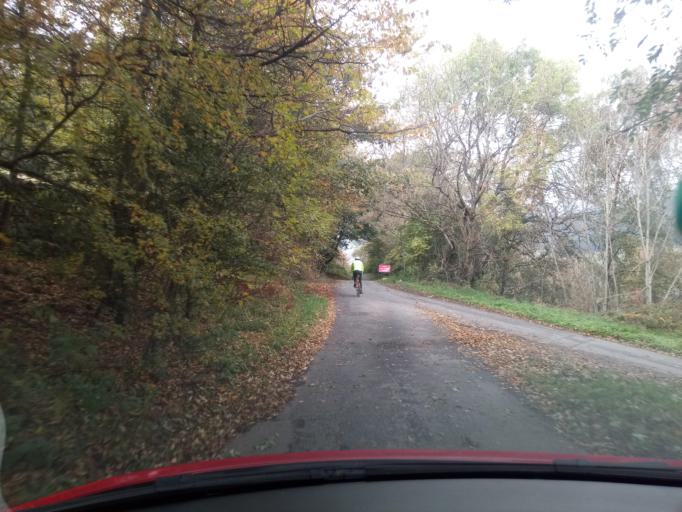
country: GB
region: Scotland
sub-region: The Scottish Borders
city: Innerleithen
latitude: 55.6192
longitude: -3.0166
